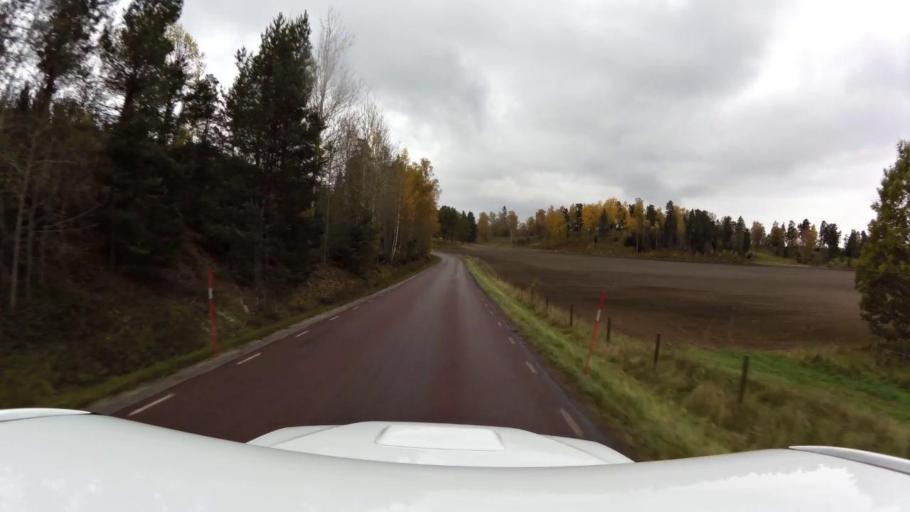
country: SE
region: OEstergoetland
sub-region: Linkopings Kommun
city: Ljungsbro
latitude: 58.5371
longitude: 15.5244
